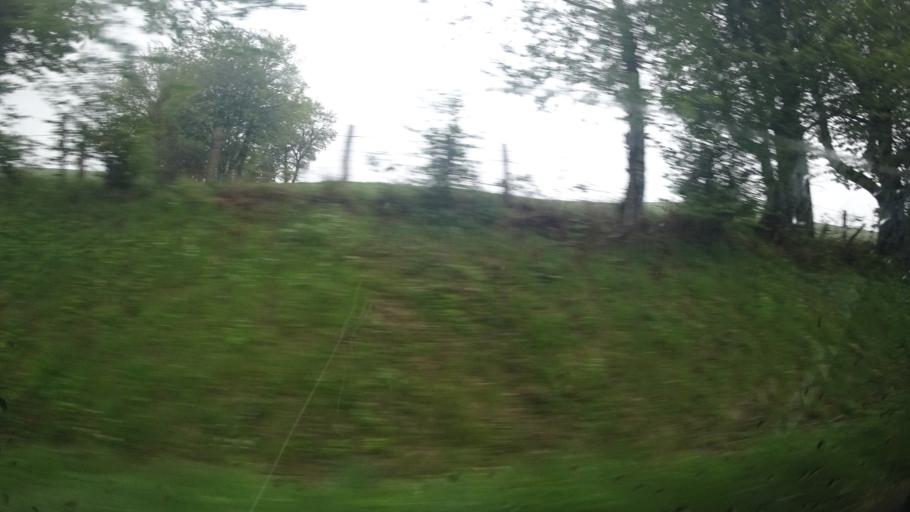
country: FR
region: Midi-Pyrenees
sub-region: Departement de l'Aveyron
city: Laissac
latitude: 44.3203
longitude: 2.7967
